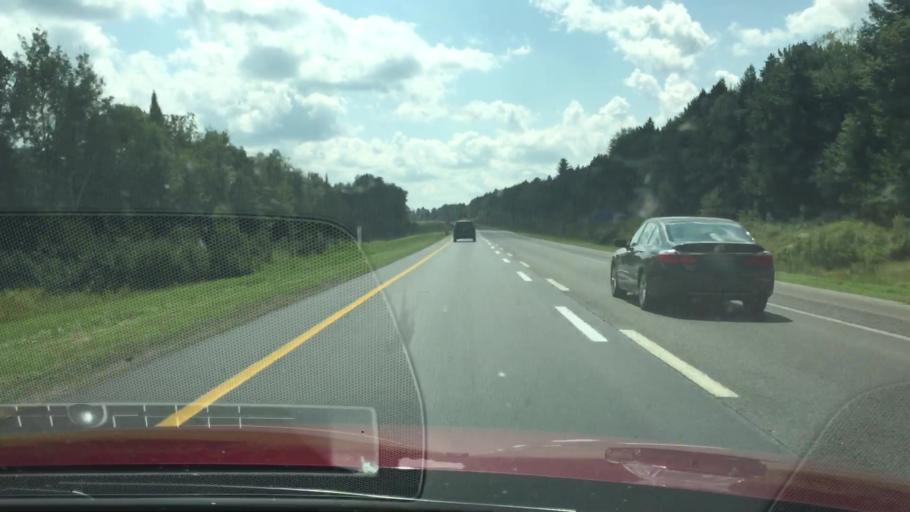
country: US
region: Maine
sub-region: Penobscot County
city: Medway
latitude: 45.6363
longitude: -68.5020
